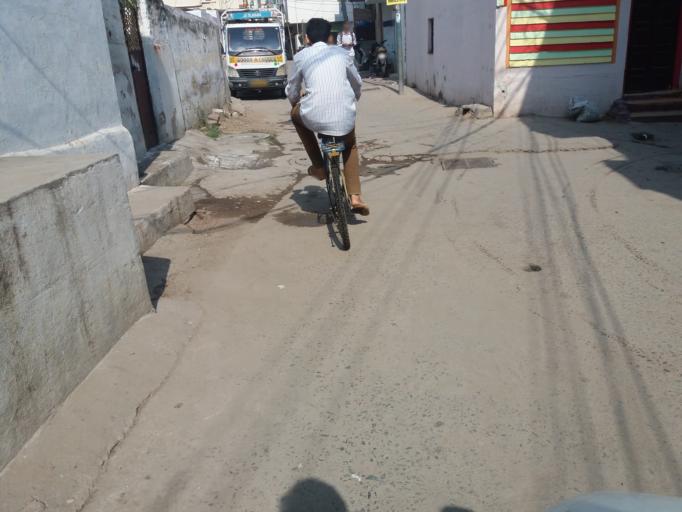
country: IN
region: Telangana
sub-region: Hyderabad
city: Malkajgiri
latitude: 17.4146
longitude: 78.5143
